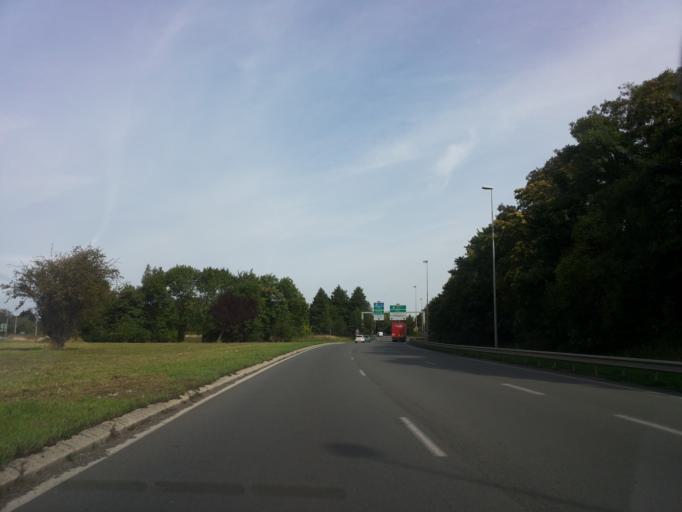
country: FR
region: Nord-Pas-de-Calais
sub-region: Departement du Pas-de-Calais
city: Saint-Nicolas
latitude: 50.3040
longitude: 2.7849
